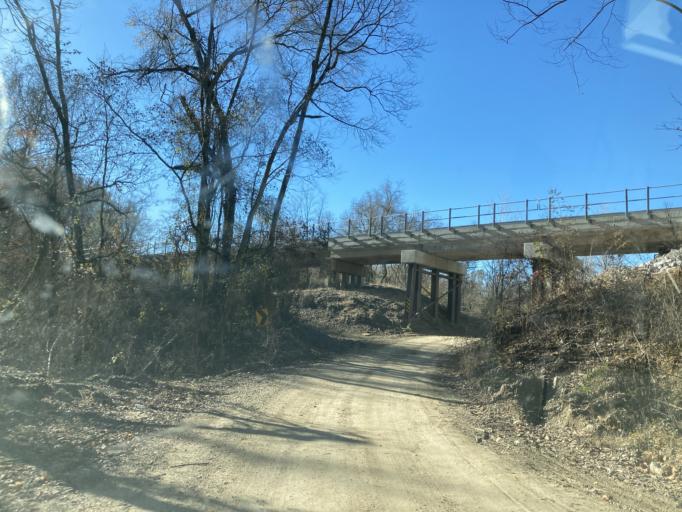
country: US
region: Mississippi
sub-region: Yazoo County
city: Yazoo City
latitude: 32.7124
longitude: -90.4154
